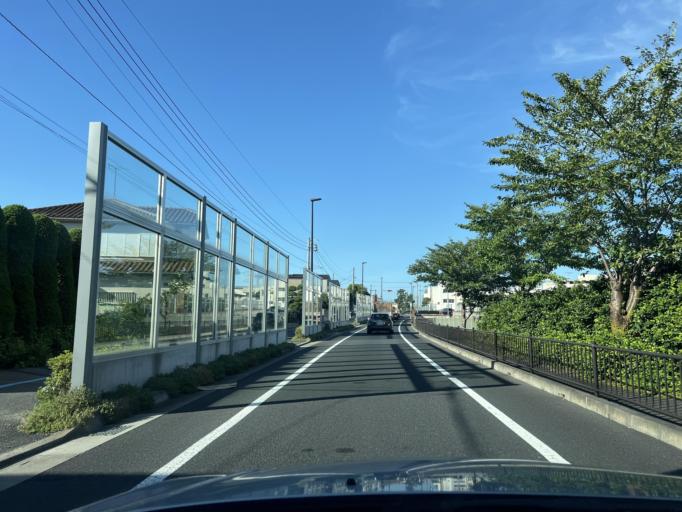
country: JP
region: Chiba
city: Funabashi
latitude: 35.7283
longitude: 139.9393
